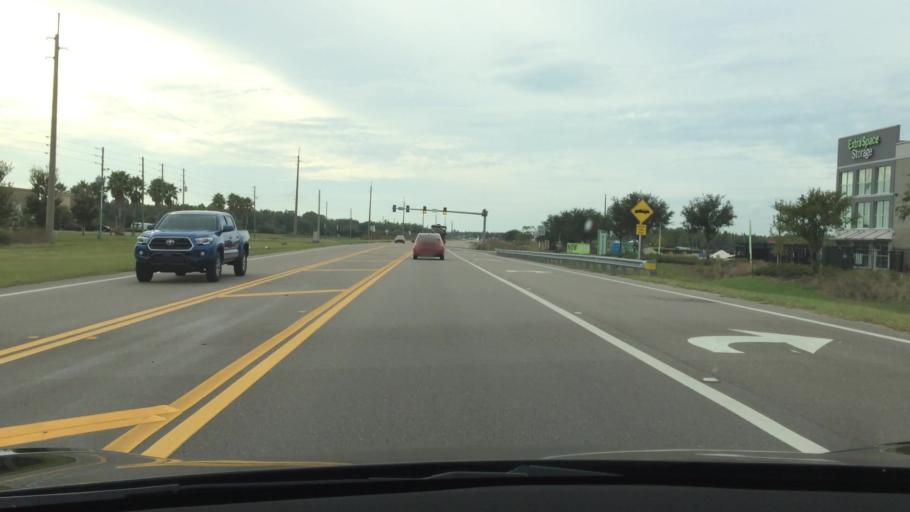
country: US
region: Florida
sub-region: Pasco County
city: Odessa
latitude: 28.1880
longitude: -82.6228
